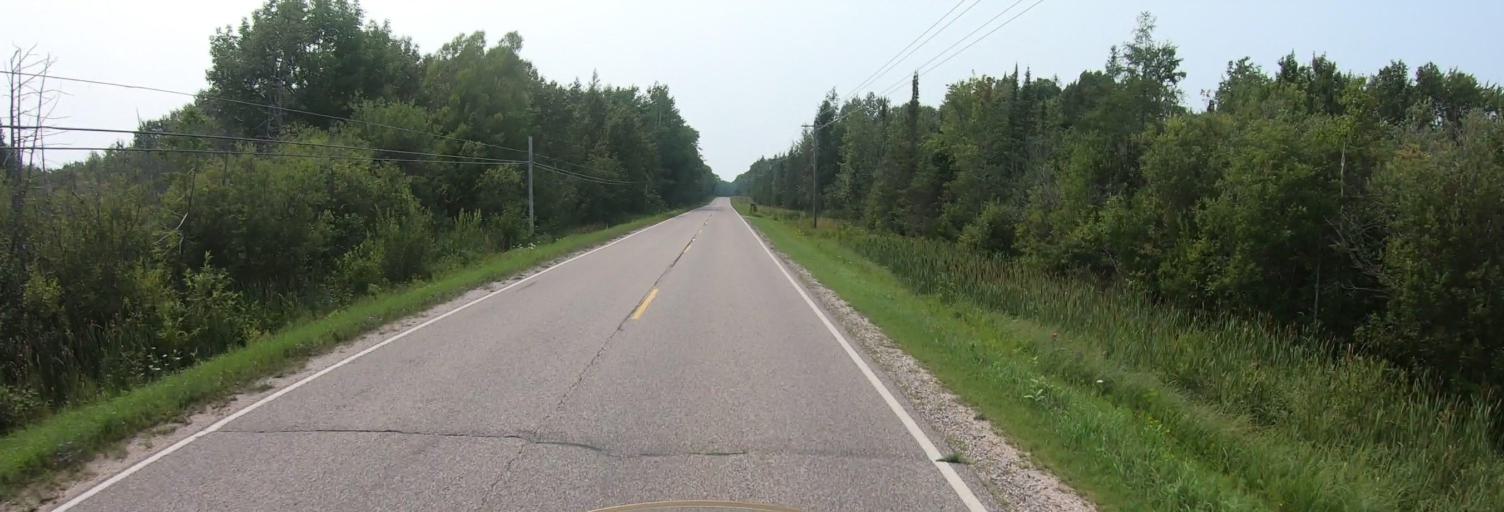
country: CA
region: Ontario
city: Thessalon
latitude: 46.0001
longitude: -83.9696
